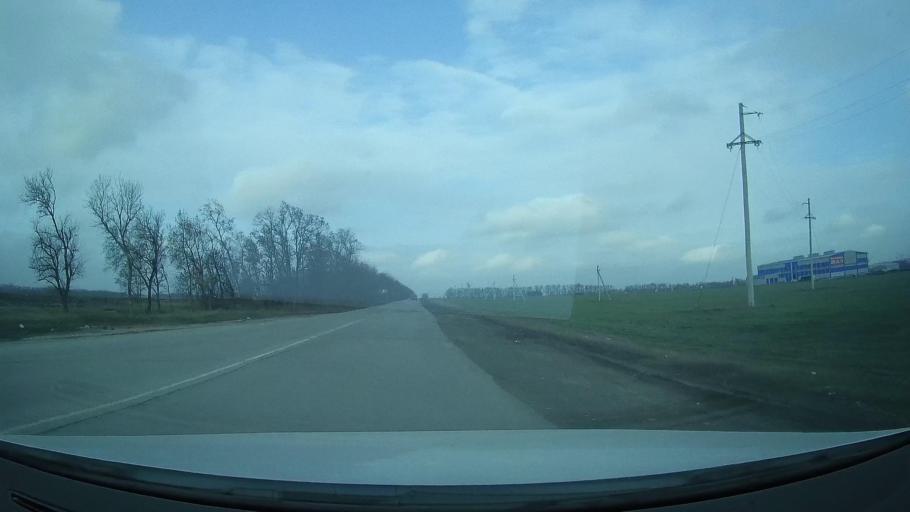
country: RU
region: Rostov
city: Temernik
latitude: 47.3788
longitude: 39.8336
